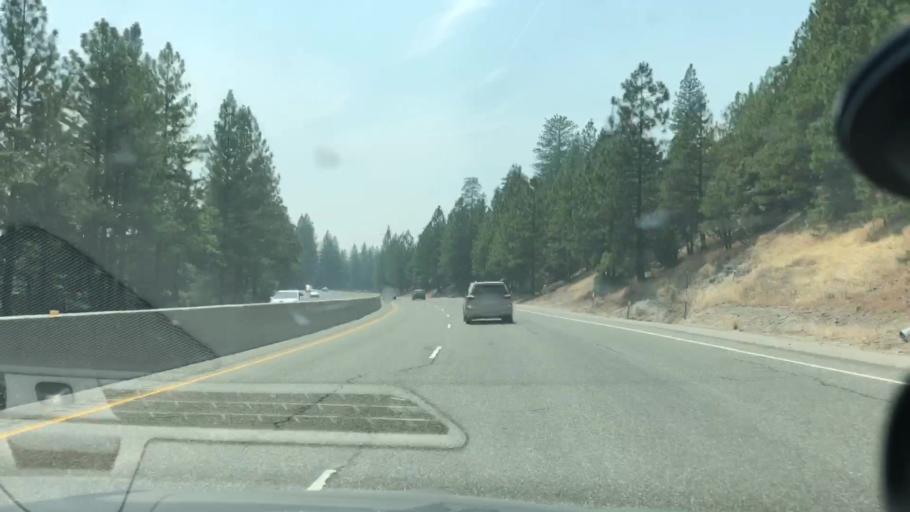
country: US
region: California
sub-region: El Dorado County
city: Pollock Pines
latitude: 38.7477
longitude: -120.6217
